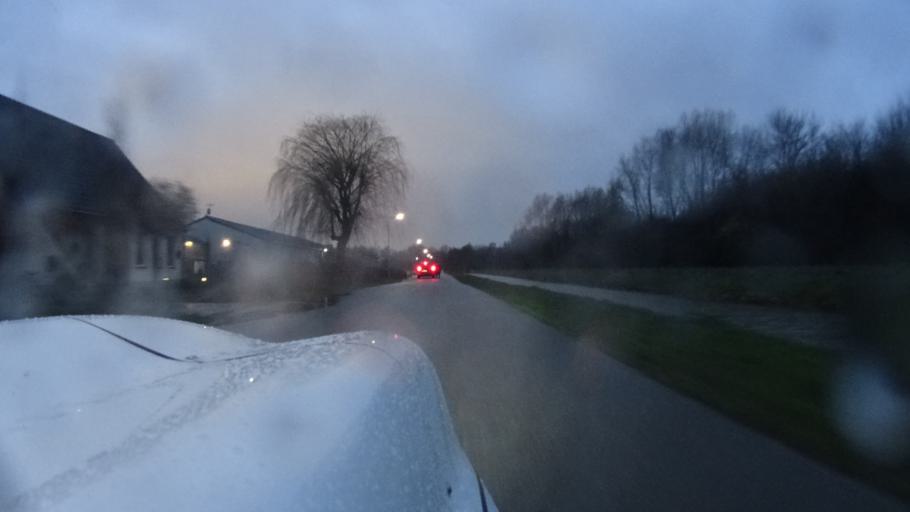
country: NL
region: South Holland
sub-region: Gemeente Pijnacker-Nootdorp
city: Pijnacker
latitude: 52.0326
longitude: 4.4352
